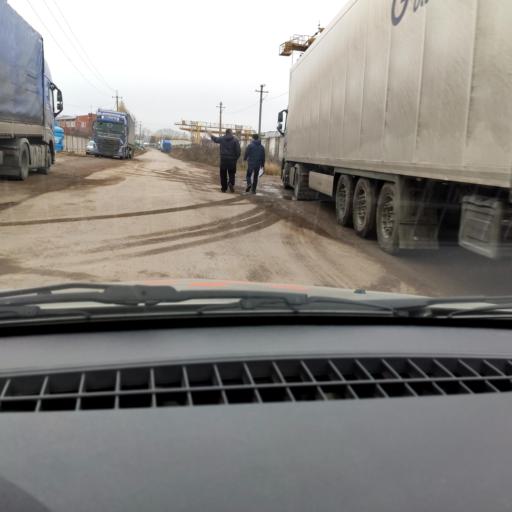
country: RU
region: Bashkortostan
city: Ufa
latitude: 54.5796
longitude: 55.8969
